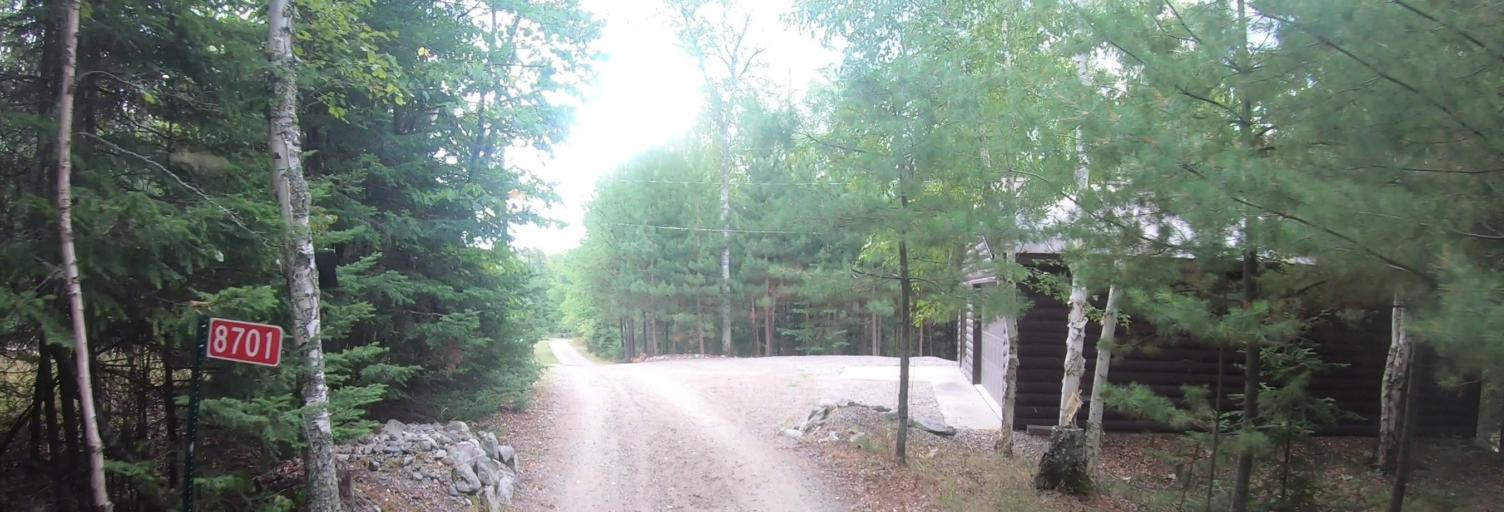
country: US
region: Minnesota
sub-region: Saint Louis County
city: Mountain Iron
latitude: 47.9448
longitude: -92.6305
